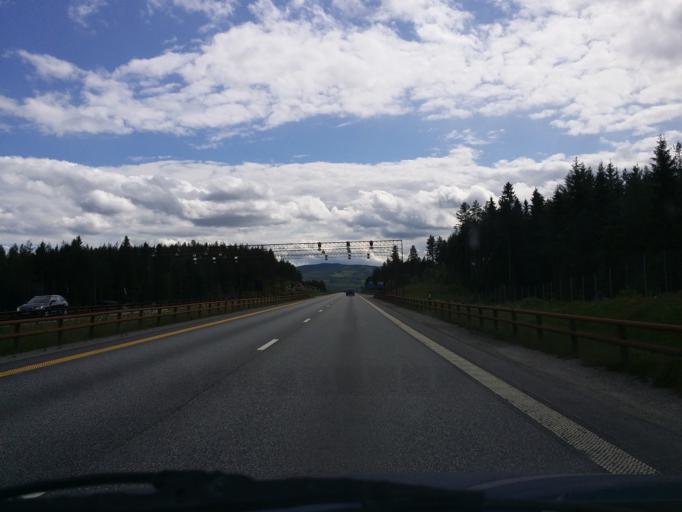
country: NO
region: Hedmark
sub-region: Stange
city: Stange
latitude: 60.6502
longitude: 11.2923
